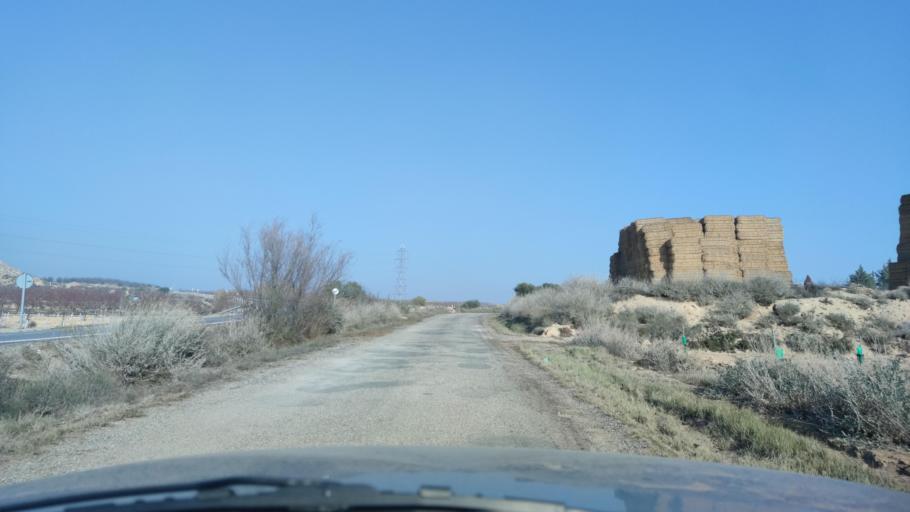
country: ES
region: Catalonia
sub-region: Provincia de Lleida
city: Seros
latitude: 41.4650
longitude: 0.3770
